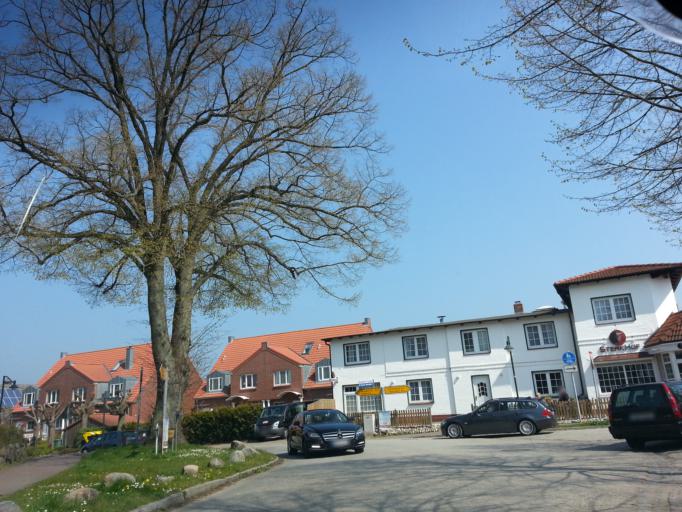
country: DE
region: Schleswig-Holstein
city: Travemuende
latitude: 53.9675
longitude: 10.8218
